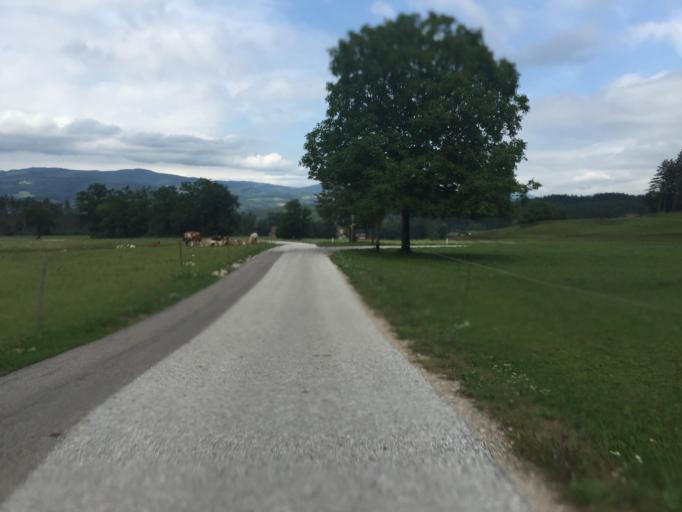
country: AT
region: Carinthia
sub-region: Politischer Bezirk Volkermarkt
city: Feistritz ob Bleiburg
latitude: 46.5458
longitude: 14.7873
